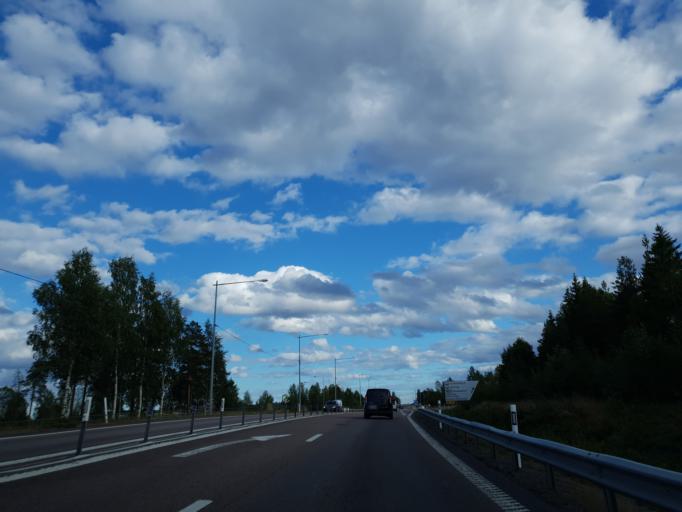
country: SE
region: Vaesternorrland
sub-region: Haernoesands Kommun
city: Haernoesand
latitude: 62.6544
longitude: 17.8815
